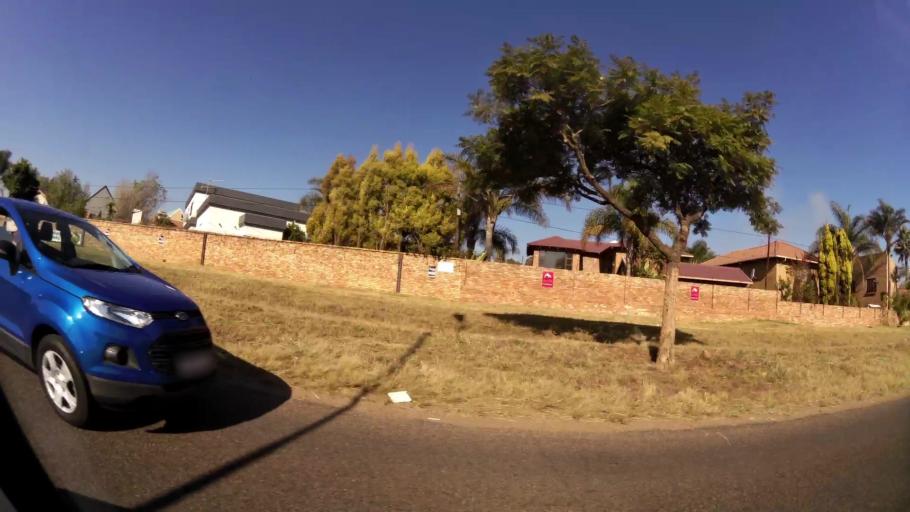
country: ZA
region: Gauteng
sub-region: City of Tshwane Metropolitan Municipality
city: Centurion
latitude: -25.8380
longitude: 28.2846
